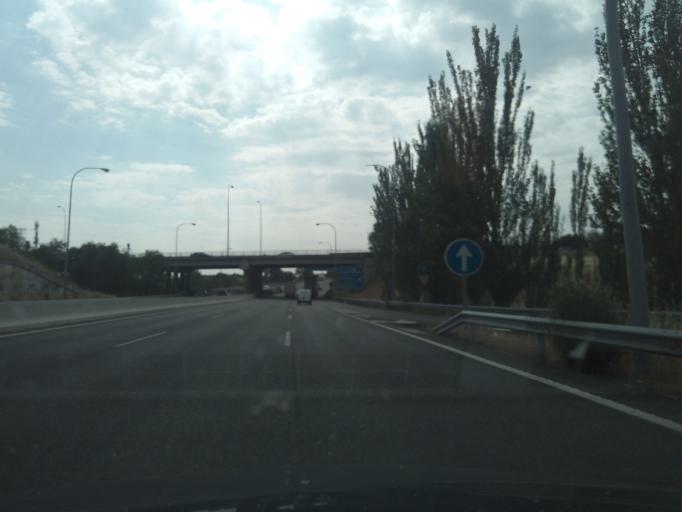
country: ES
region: Madrid
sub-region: Provincia de Madrid
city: San Blas
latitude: 40.4421
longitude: -3.5936
